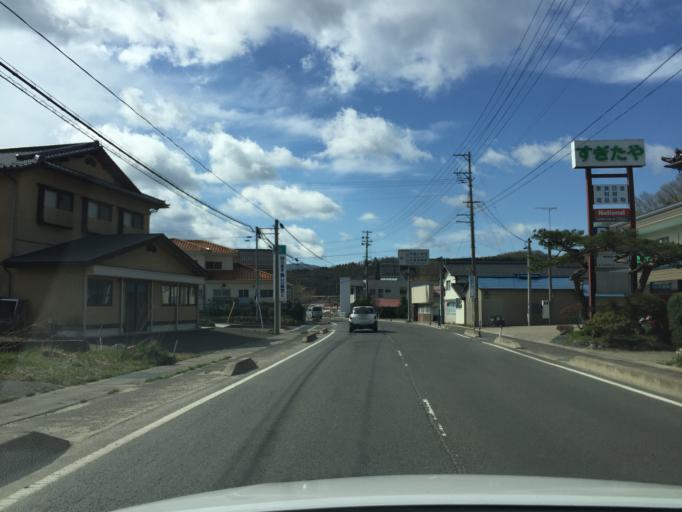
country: JP
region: Fukushima
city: Funehikimachi-funehiki
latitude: 37.6036
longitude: 140.6729
